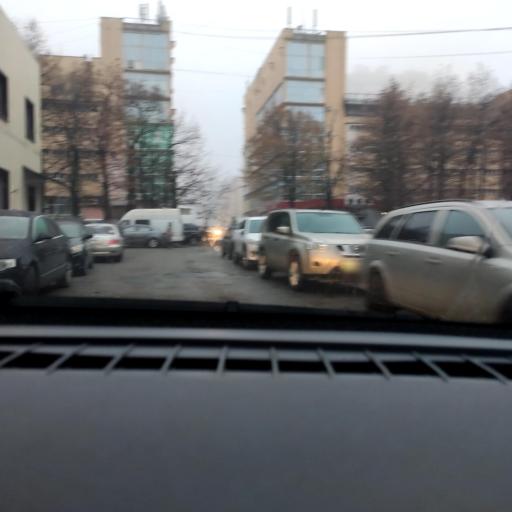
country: RU
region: Voronezj
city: Voronezh
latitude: 51.7121
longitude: 39.1864
